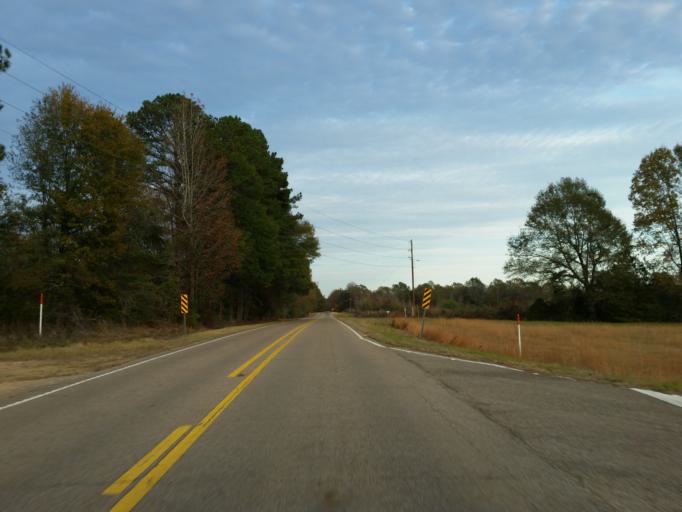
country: US
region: Mississippi
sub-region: Lauderdale County
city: Marion
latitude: 32.4239
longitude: -88.4741
